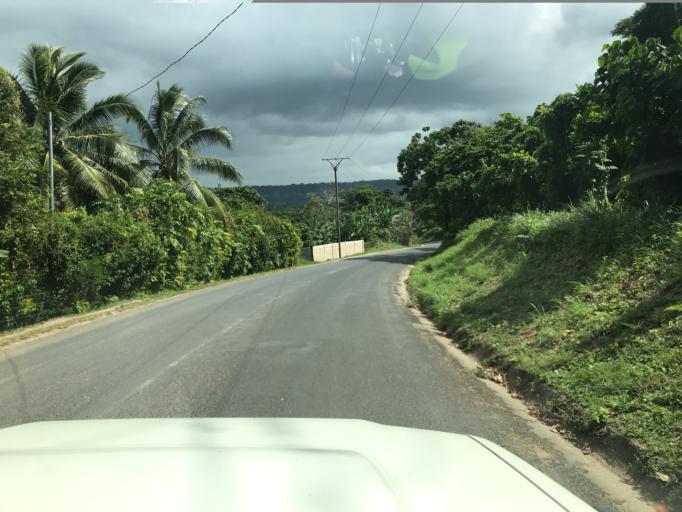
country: VU
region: Sanma
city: Luganville
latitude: -15.5105
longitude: 167.1796
